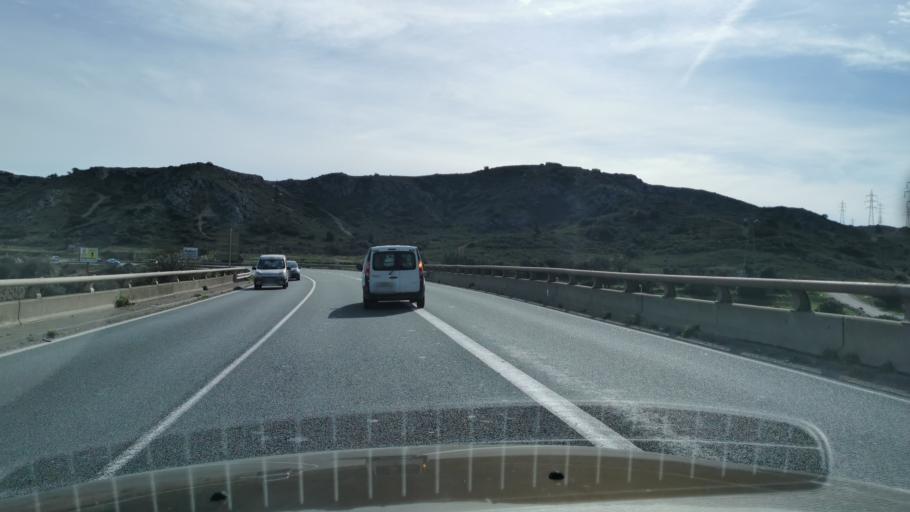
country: FR
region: Languedoc-Roussillon
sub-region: Departement de l'Aude
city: Narbonne
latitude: 43.1804
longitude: 2.9675
